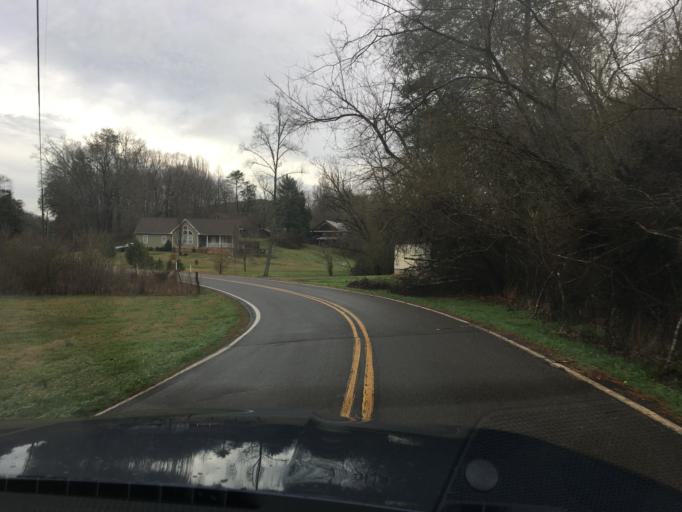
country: US
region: Tennessee
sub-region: McMinn County
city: Englewood
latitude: 35.3815
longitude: -84.4372
